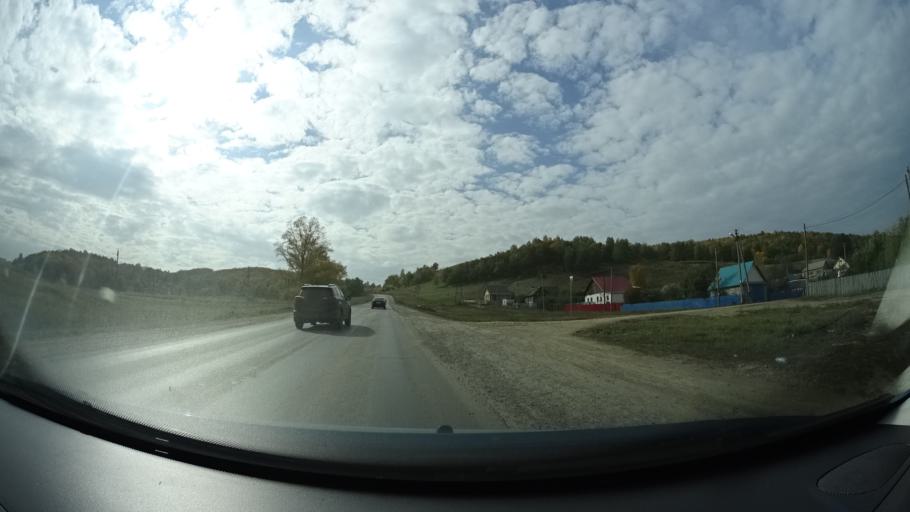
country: RU
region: Bashkortostan
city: Tuymazy
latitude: 54.5515
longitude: 53.5882
